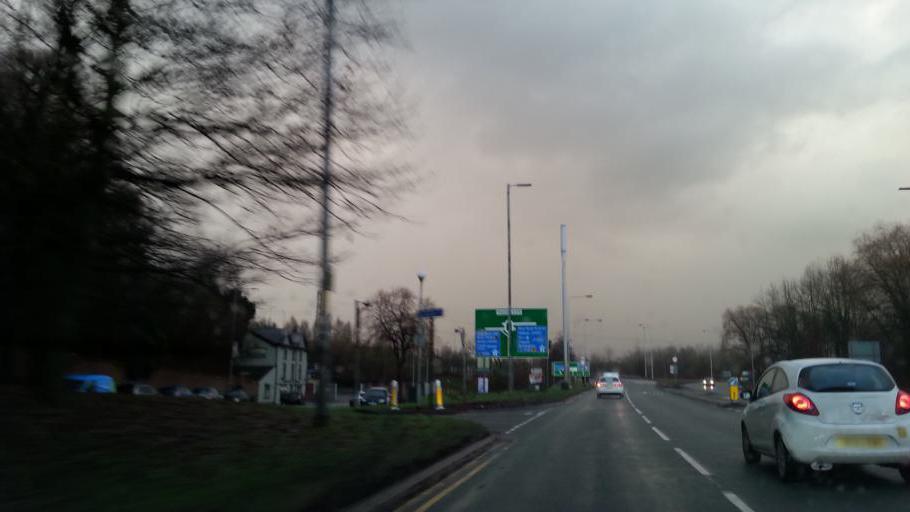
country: GB
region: England
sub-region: Manchester
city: Crumpsall
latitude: 53.5382
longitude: -2.2403
